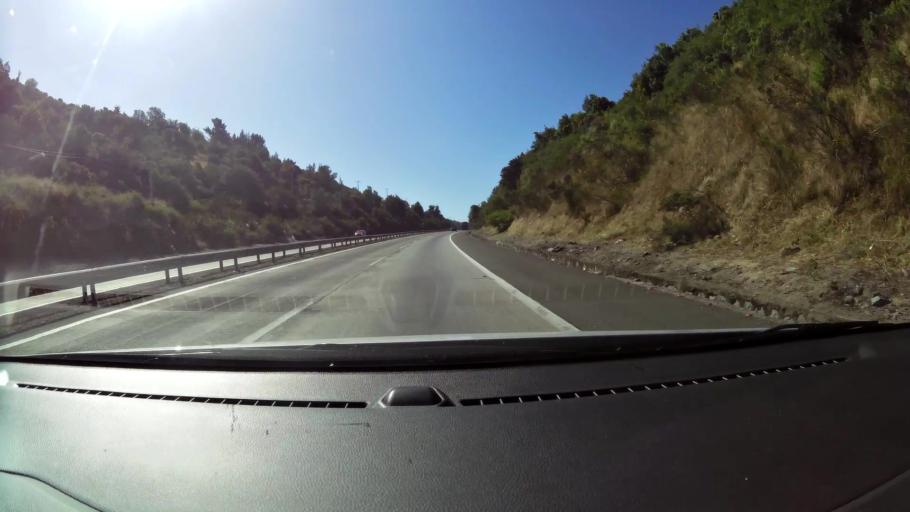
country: CL
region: Valparaiso
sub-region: Provincia de Marga Marga
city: Quilpue
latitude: -33.2363
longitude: -71.4601
